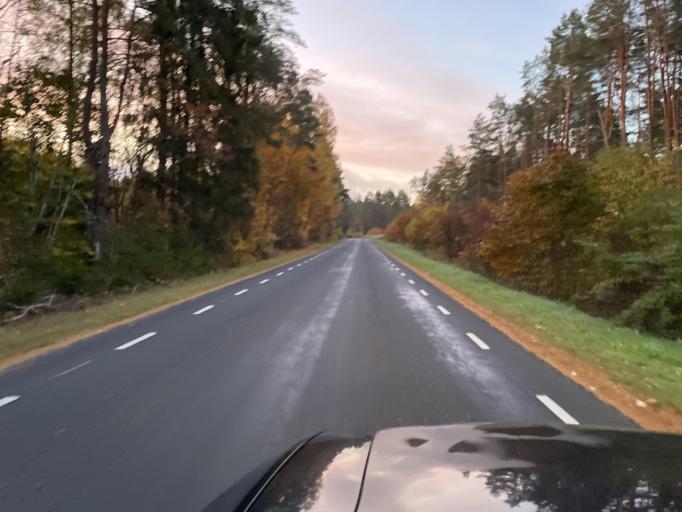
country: EE
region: Harju
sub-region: Nissi vald
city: Riisipere
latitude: 59.2535
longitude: 24.2305
